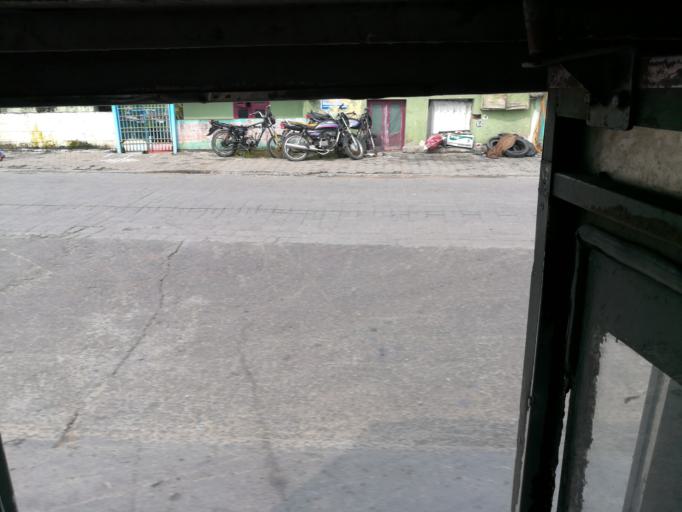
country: IN
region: Tamil Nadu
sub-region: Kancheepuram
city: Injambakkam
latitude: 12.9083
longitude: 80.2283
